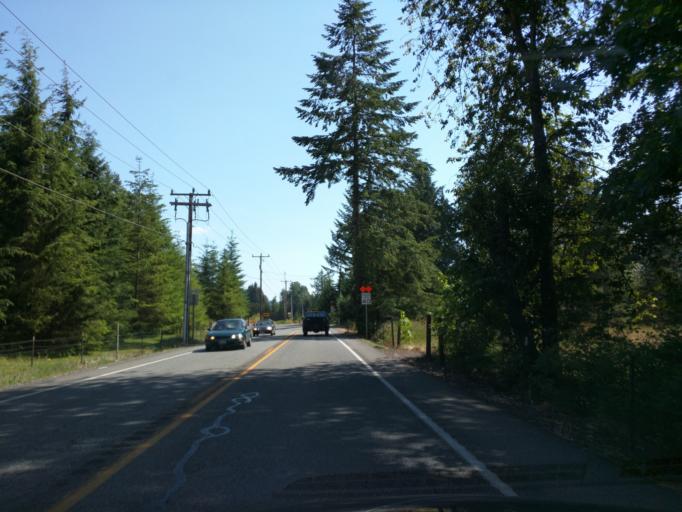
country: US
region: Washington
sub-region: Whatcom County
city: Peaceful Valley
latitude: 48.9184
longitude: -122.1433
